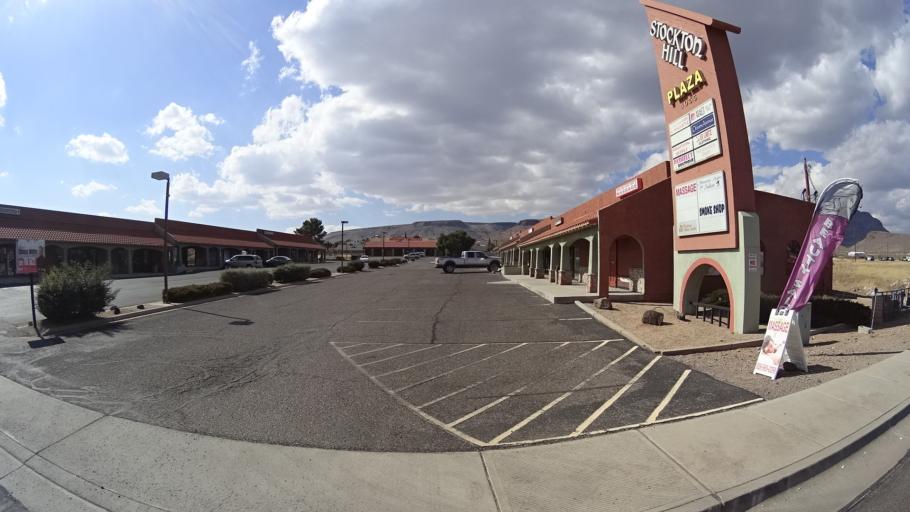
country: US
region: Arizona
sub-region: Mohave County
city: New Kingman-Butler
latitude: 35.2412
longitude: -114.0381
